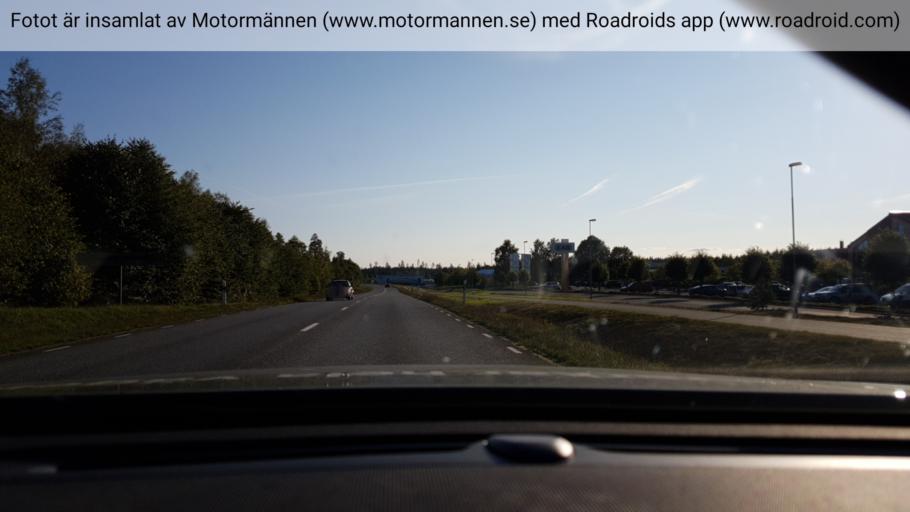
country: SE
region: Joenkoeping
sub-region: Gislaveds Kommun
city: Smalandsstenar
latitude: 57.1444
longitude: 13.3875
